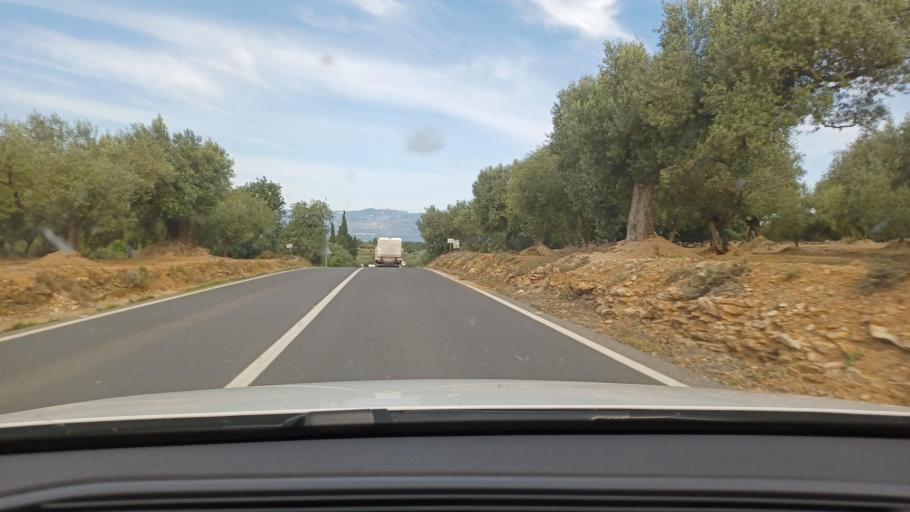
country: ES
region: Catalonia
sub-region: Provincia de Tarragona
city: Masdenverge
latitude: 40.7081
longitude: 0.5448
